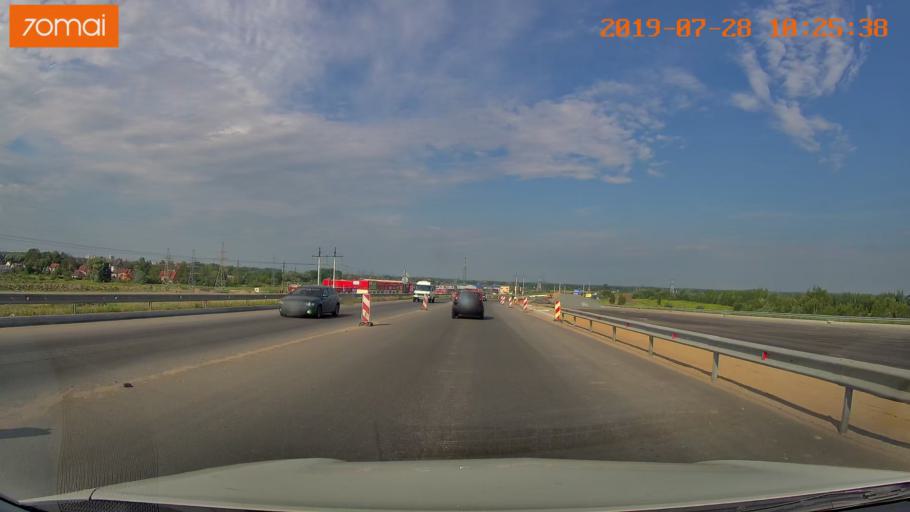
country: RU
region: Kaliningrad
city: Maloye Isakovo
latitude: 54.7678
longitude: 20.5396
